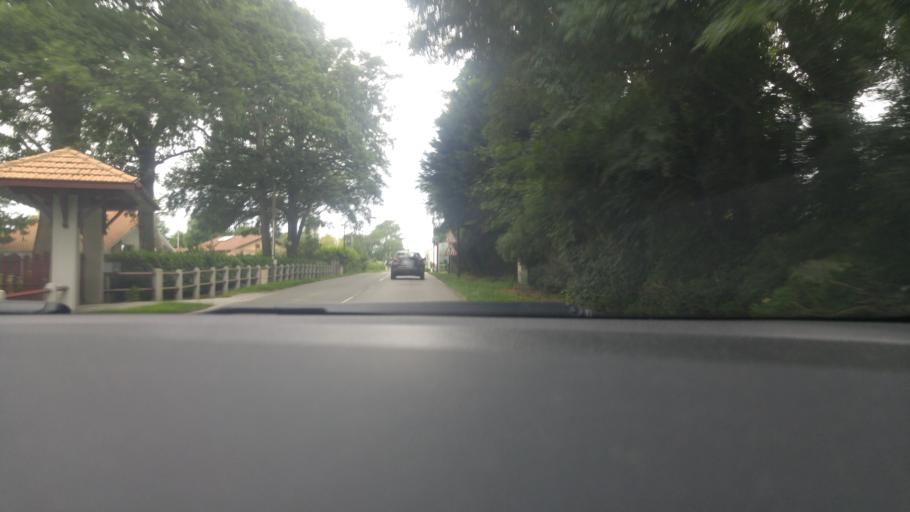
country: FR
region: Aquitaine
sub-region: Departement des Landes
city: Soustons
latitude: 43.7475
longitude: -1.3173
